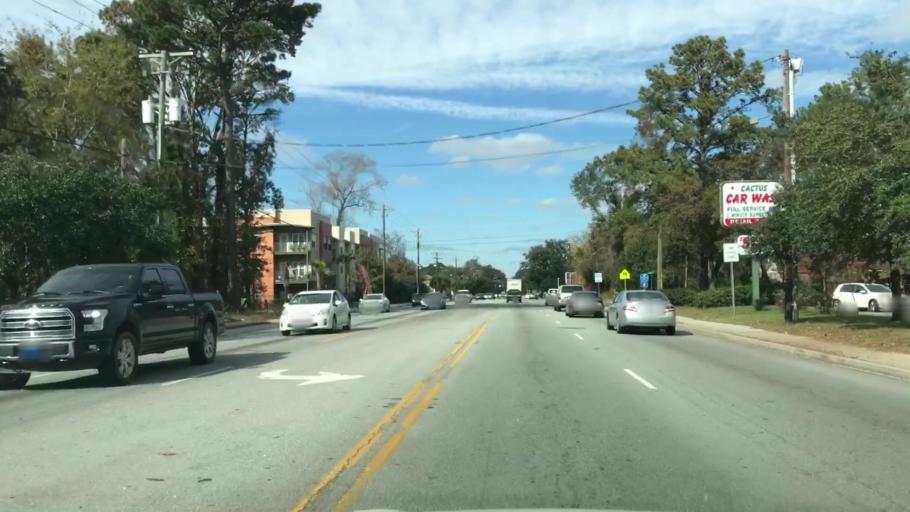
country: US
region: South Carolina
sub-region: Charleston County
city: North Charleston
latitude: 32.8040
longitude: -80.0195
